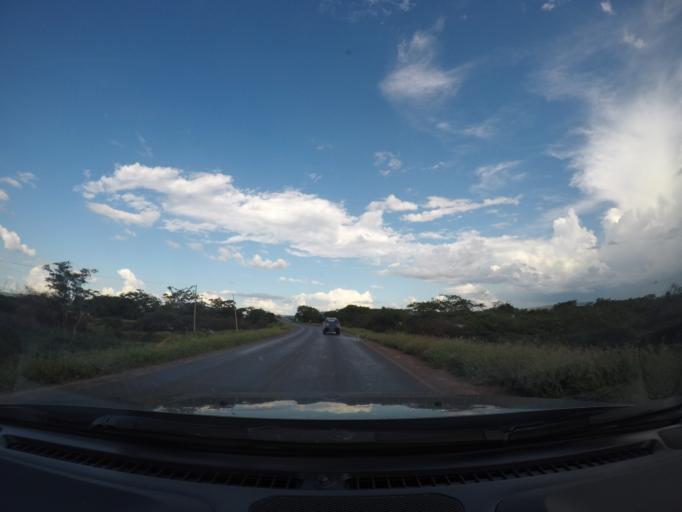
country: BR
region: Bahia
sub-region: Ibotirama
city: Ibotirama
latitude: -12.1821
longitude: -43.2330
